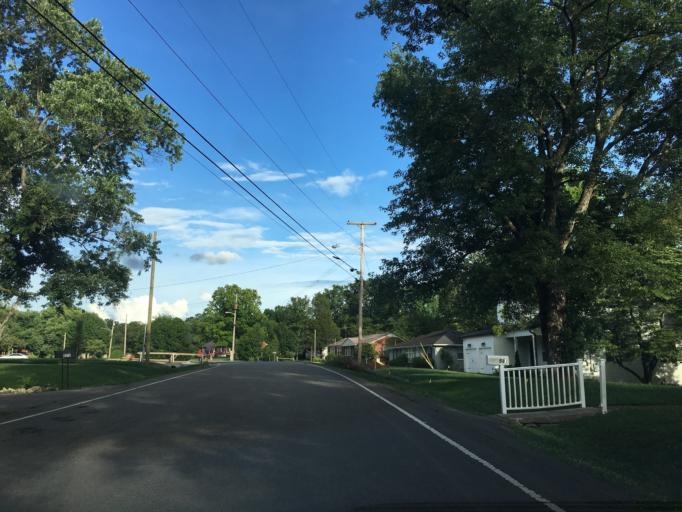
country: US
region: Tennessee
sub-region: Davidson County
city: Oak Hill
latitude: 36.0635
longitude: -86.7312
